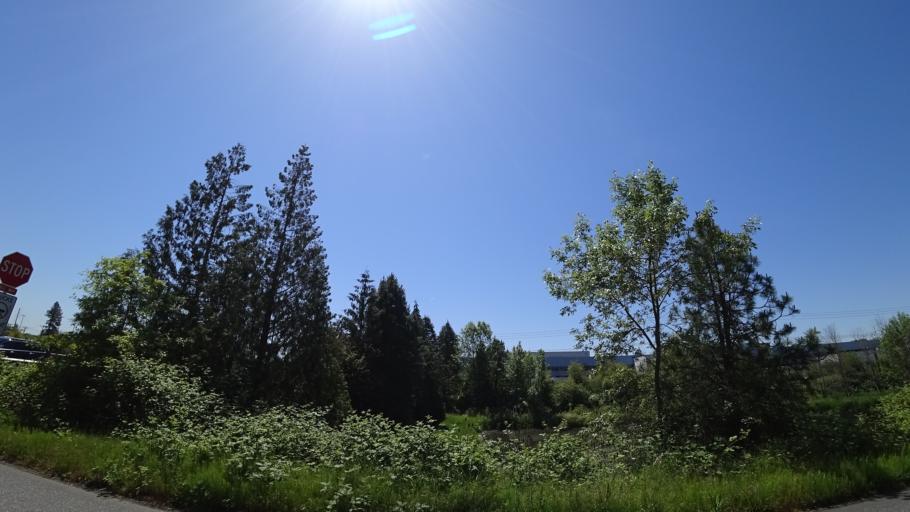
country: US
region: Oregon
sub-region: Washington County
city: Beaverton
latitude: 45.4969
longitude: -122.8235
